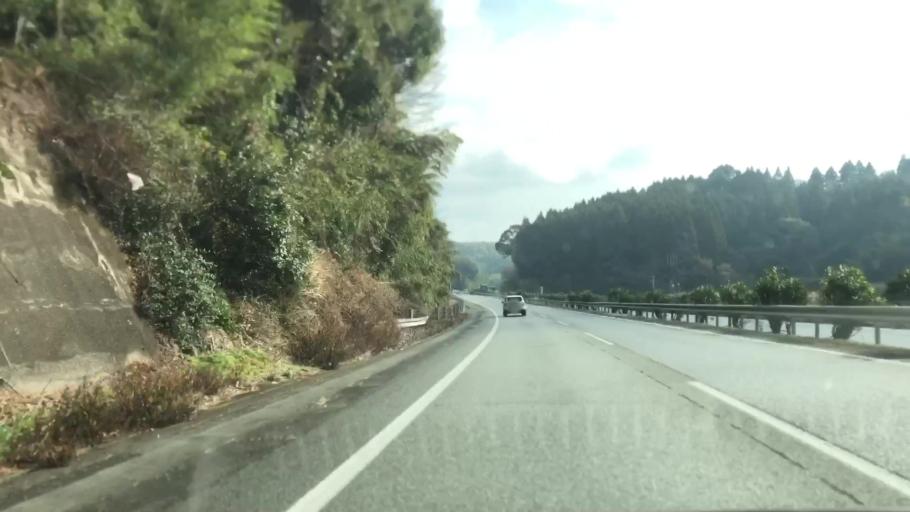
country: JP
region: Kumamoto
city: Yamaga
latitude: 33.0318
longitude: 130.5735
